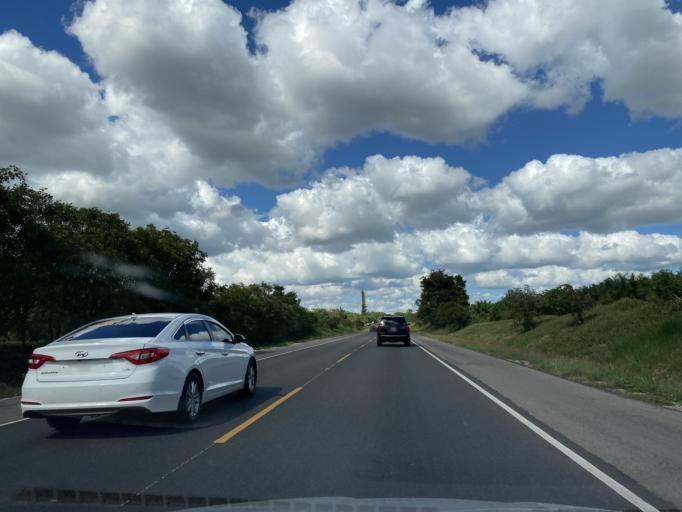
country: DO
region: Monte Plata
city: Monte Plata
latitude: 18.7405
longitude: -69.7638
